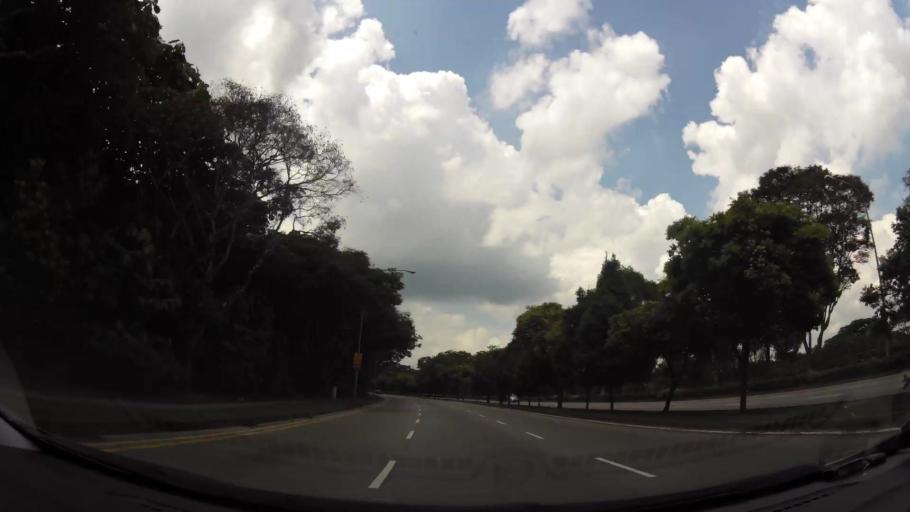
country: MY
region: Johor
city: Kampung Pasir Gudang Baru
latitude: 1.4140
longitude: 103.8218
